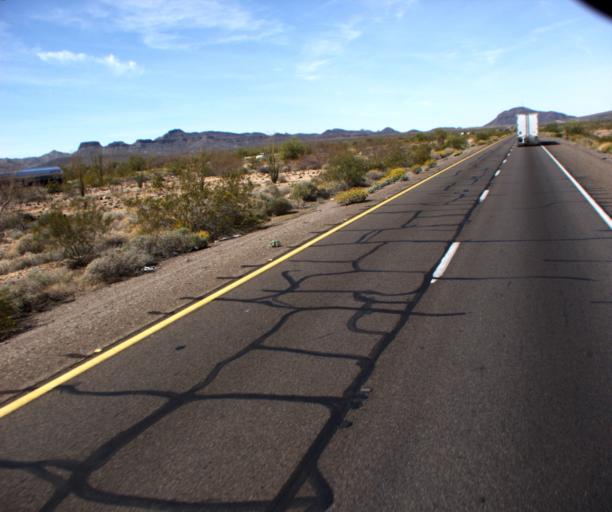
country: US
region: Arizona
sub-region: La Paz County
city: Quartzsite
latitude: 33.6575
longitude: -113.9735
